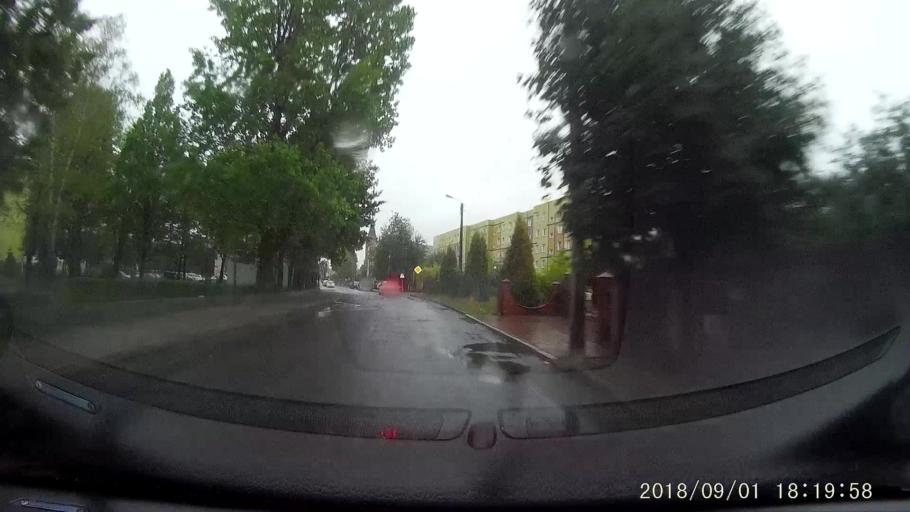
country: PL
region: Lower Silesian Voivodeship
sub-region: Powiat zgorzelecki
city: Piensk
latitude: 51.2521
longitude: 15.0448
